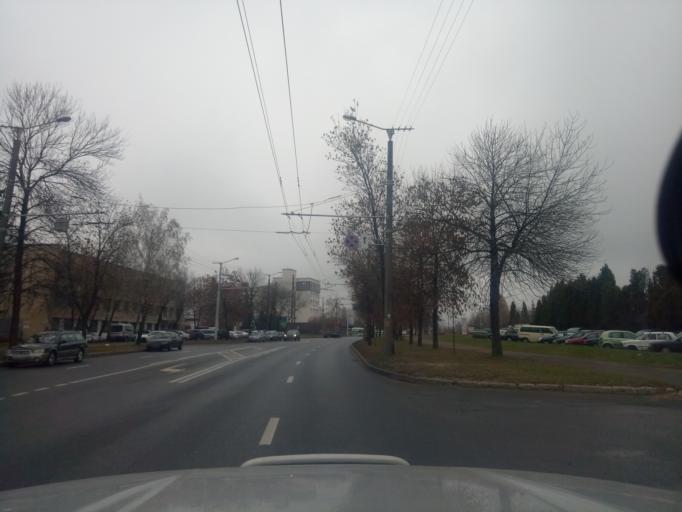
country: BY
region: Minsk
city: Novoye Medvezhino
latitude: 53.8831
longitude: 27.4824
